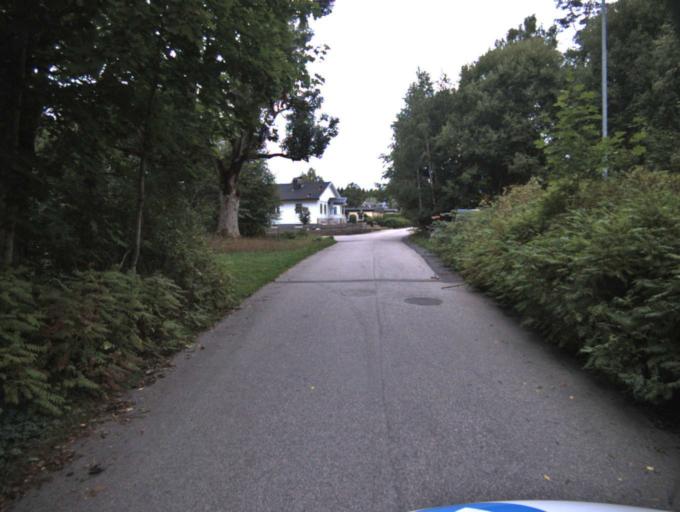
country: SE
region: Vaestra Goetaland
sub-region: Boras Kommun
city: Dalsjofors
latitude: 57.8279
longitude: 13.1963
